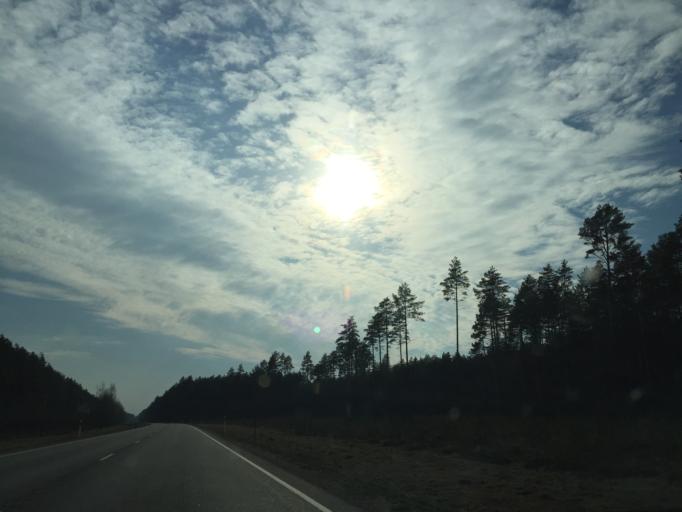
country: EE
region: Jogevamaa
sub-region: Mustvee linn
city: Mustvee
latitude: 58.9666
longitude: 27.1057
